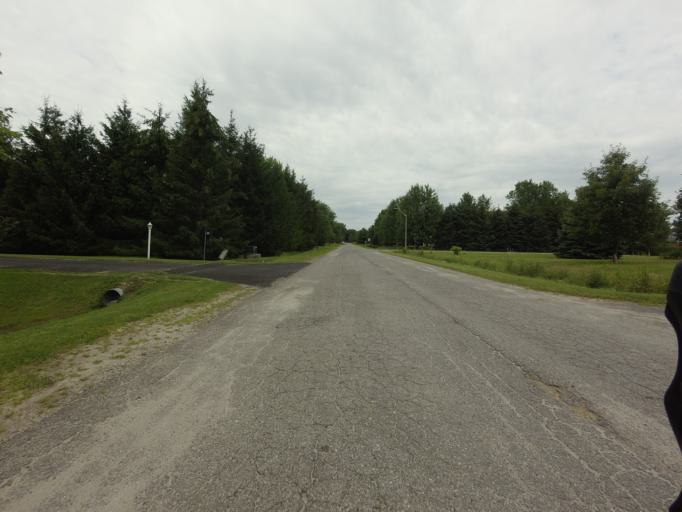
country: CA
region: Ontario
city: Bells Corners
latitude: 45.0243
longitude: -75.6914
